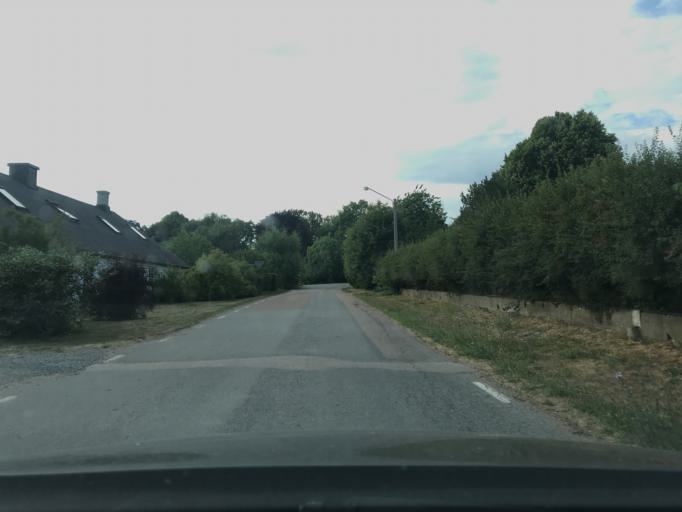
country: SE
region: Skane
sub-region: Simrishamns Kommun
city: Kivik
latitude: 55.5249
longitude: 14.1668
